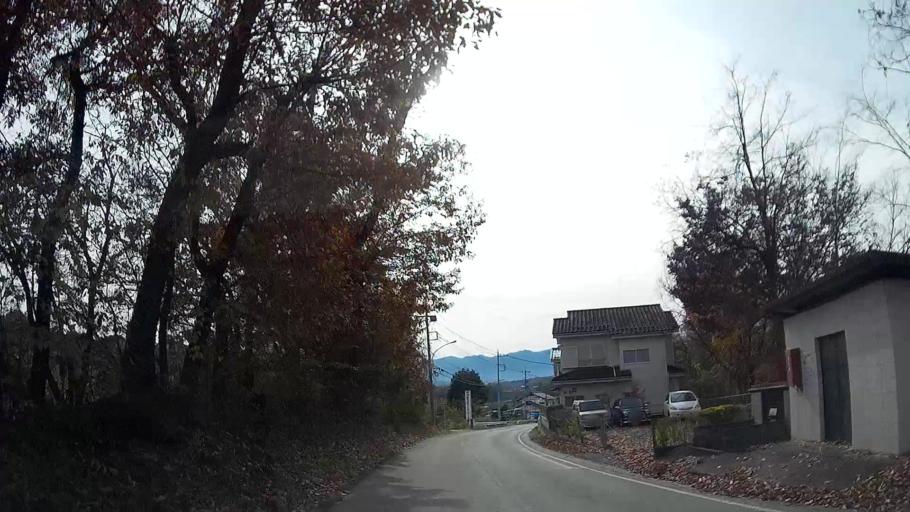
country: JP
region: Saitama
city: Chichibu
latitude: 36.0450
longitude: 139.0391
